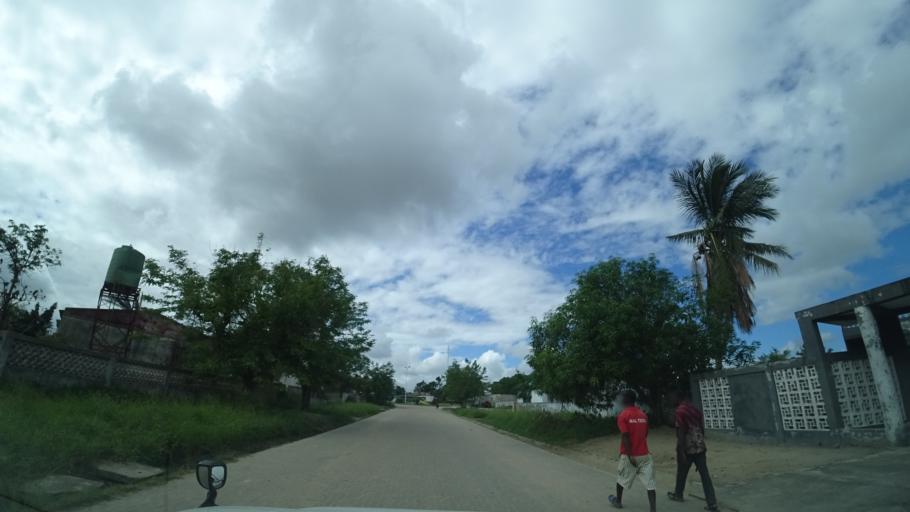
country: MZ
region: Sofala
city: Dondo
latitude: -19.6172
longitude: 34.7450
